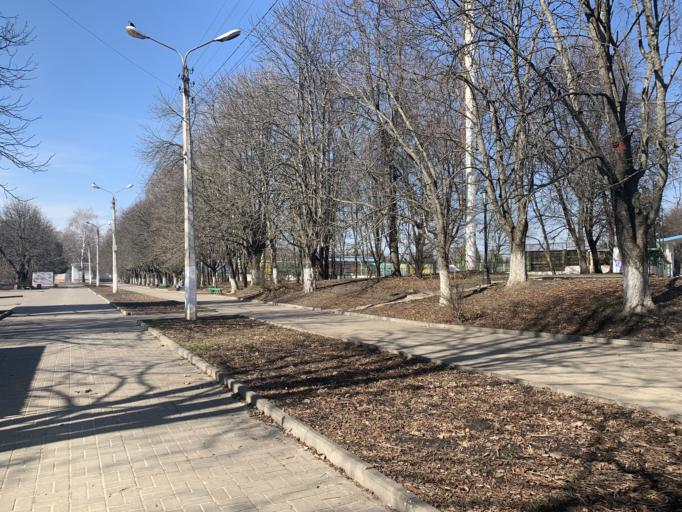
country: RU
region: Kursk
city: Zheleznogorsk
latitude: 52.3261
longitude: 35.3601
